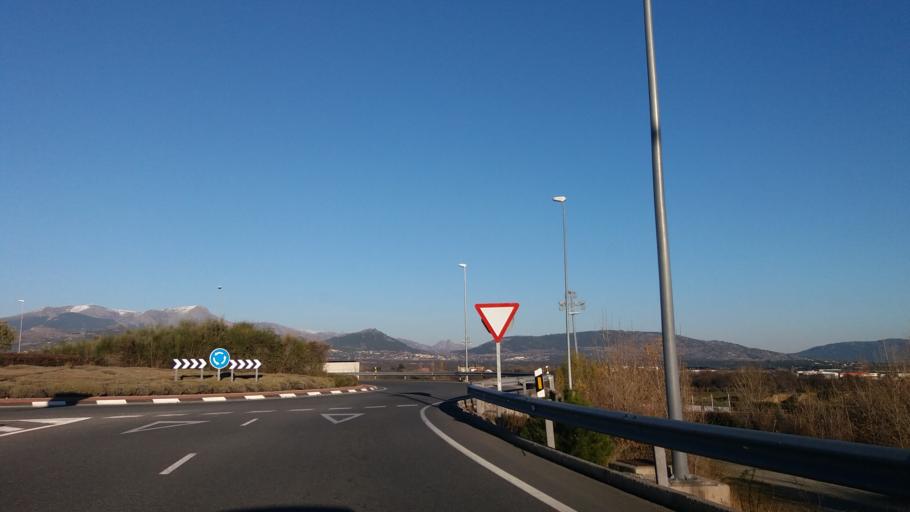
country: ES
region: Madrid
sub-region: Provincia de Madrid
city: Guadarrama
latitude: 40.6622
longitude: -4.0918
